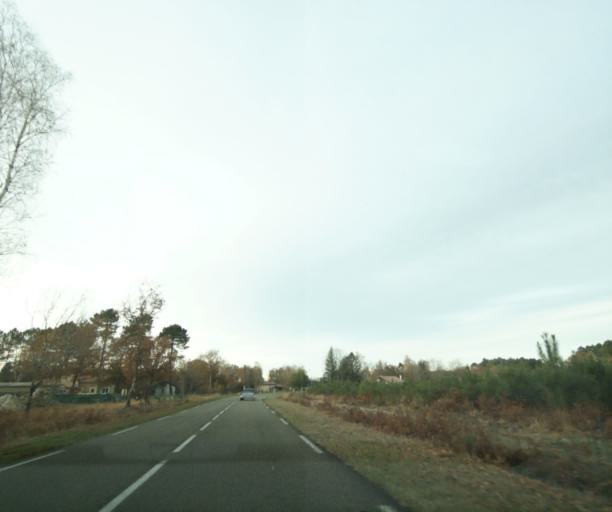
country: FR
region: Aquitaine
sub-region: Departement de la Gironde
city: Bazas
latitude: 44.2760
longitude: -0.2478
